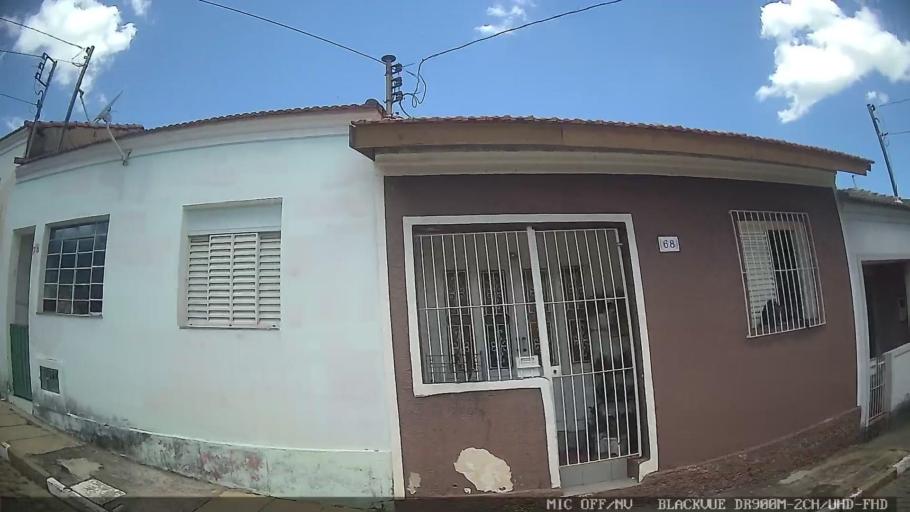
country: BR
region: Sao Paulo
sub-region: Atibaia
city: Atibaia
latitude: -23.1094
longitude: -46.5569
